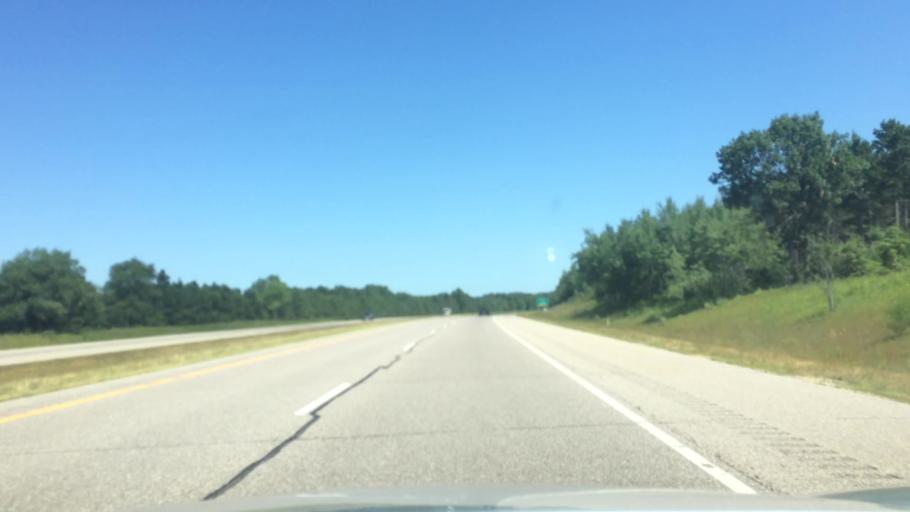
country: US
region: Wisconsin
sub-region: Marquette County
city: Westfield
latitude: 44.0573
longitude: -89.5421
